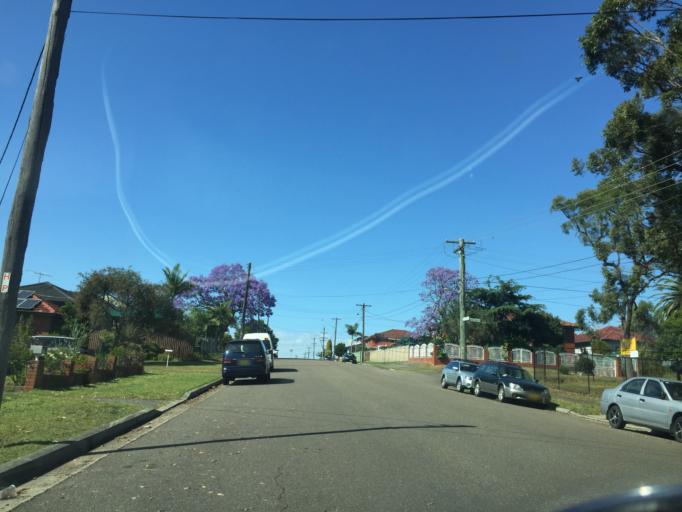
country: AU
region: New South Wales
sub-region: Fairfield
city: Fairfield Heights
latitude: -33.8528
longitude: 150.9317
